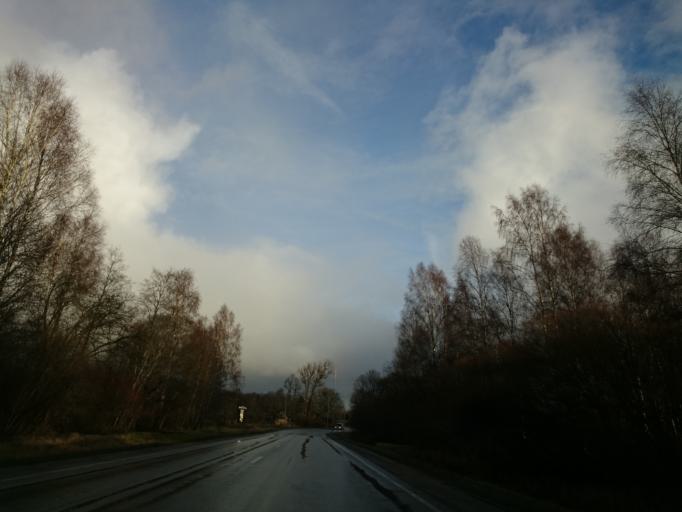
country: LV
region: Skrunda
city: Skrunda
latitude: 56.6718
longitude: 21.9912
